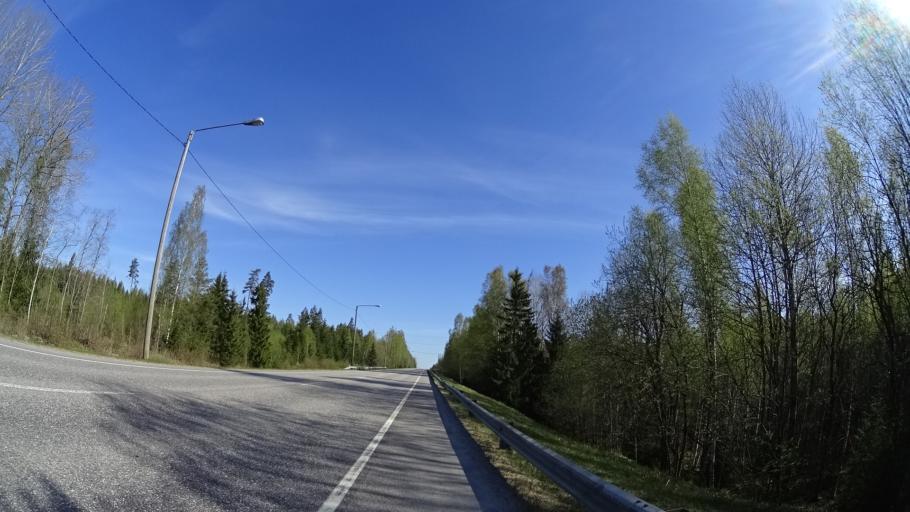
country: FI
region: Uusimaa
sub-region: Helsinki
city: Nurmijaervi
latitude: 60.3793
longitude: 24.8067
